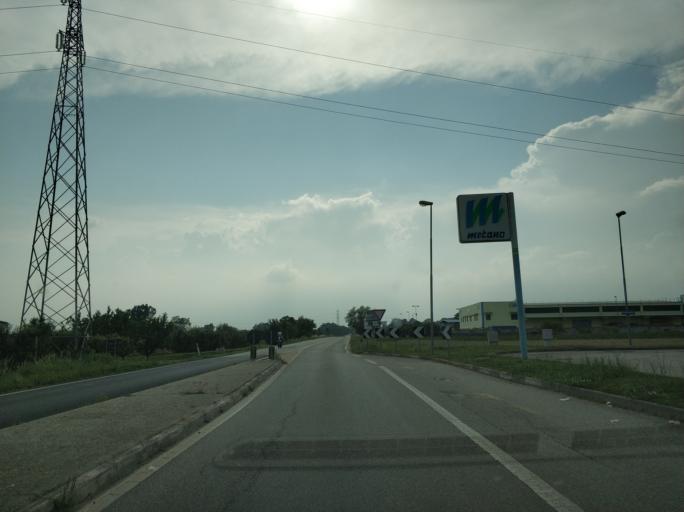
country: IT
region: Piedmont
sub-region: Provincia di Torino
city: Caluso
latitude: 45.3080
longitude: 7.8737
